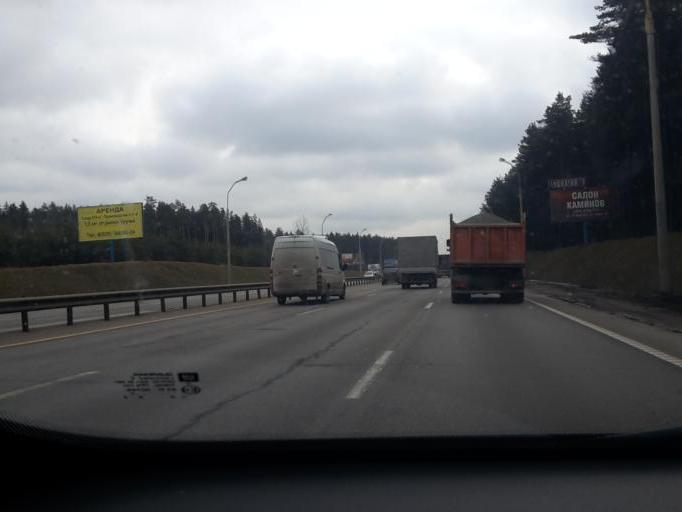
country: BY
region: Minsk
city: Borovlyany
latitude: 53.9518
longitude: 27.6495
